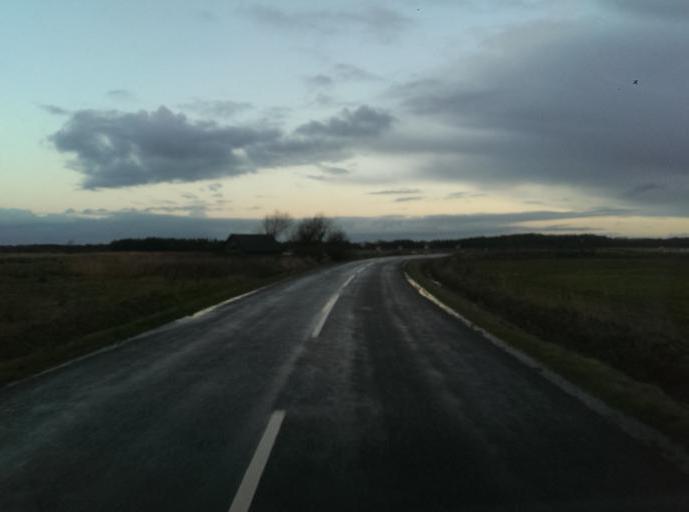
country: DK
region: South Denmark
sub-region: Esbjerg Kommune
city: Tjaereborg
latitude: 55.4596
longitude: 8.6398
